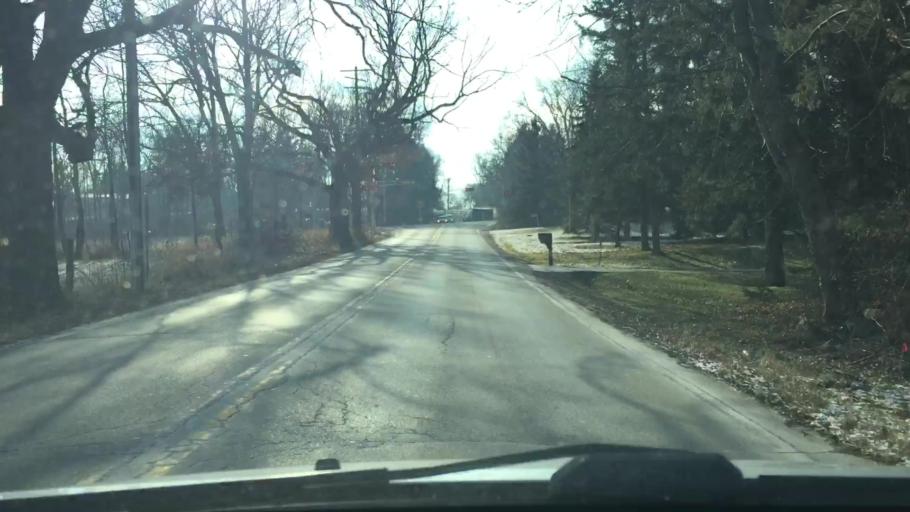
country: US
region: Wisconsin
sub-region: Waukesha County
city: Waukesha
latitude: 42.9897
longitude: -88.2890
